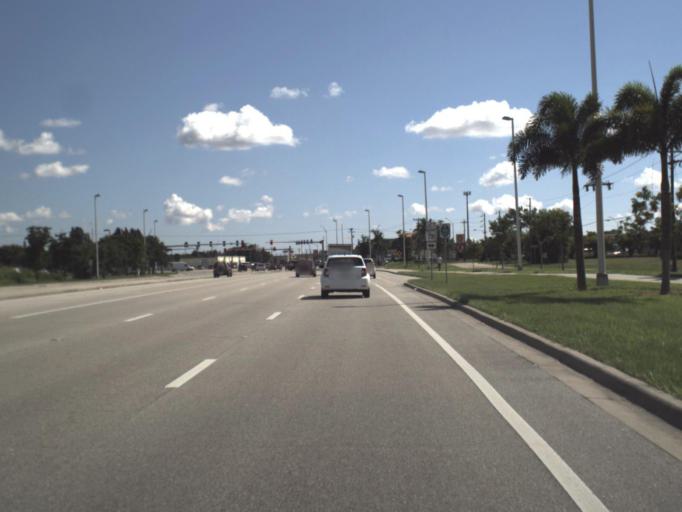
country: US
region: Florida
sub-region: Lee County
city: Lochmoor Waterway Estates
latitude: 26.6704
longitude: -81.9416
